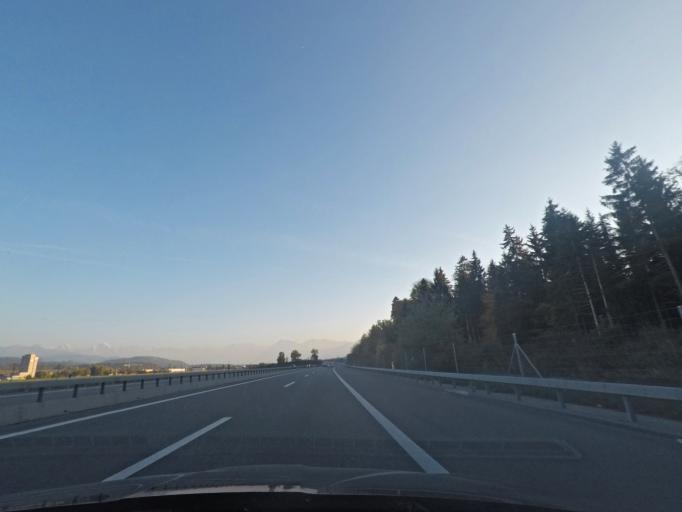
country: CH
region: Bern
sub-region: Bern-Mittelland District
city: Niederwichtrach
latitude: 46.8504
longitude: 7.5585
